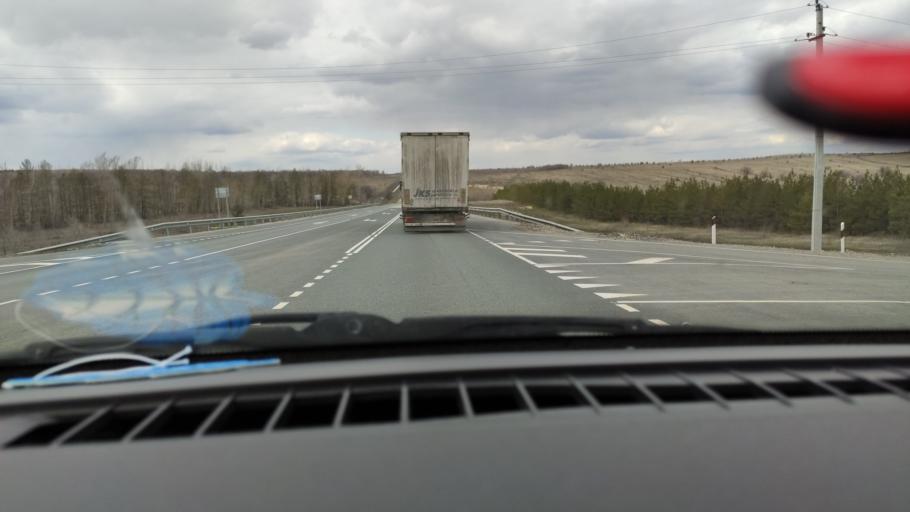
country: RU
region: Saratov
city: Shikhany
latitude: 52.1386
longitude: 47.2124
